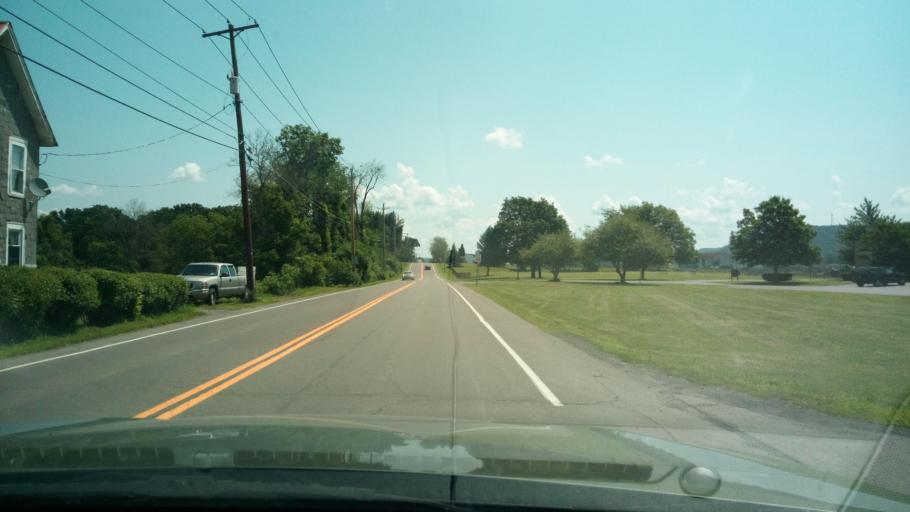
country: US
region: New York
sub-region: Chemung County
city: Horseheads North
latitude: 42.1902
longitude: -76.8254
